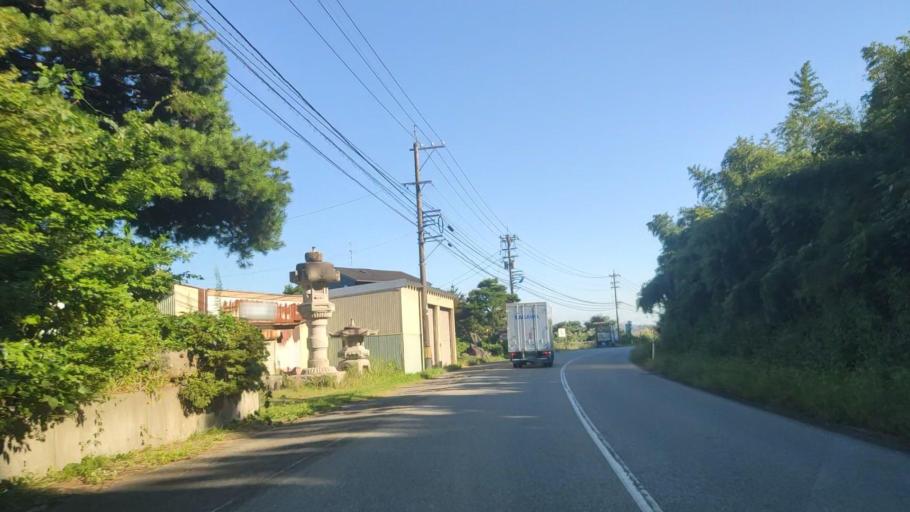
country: JP
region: Ishikawa
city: Nanao
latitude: 37.1991
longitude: 136.9091
